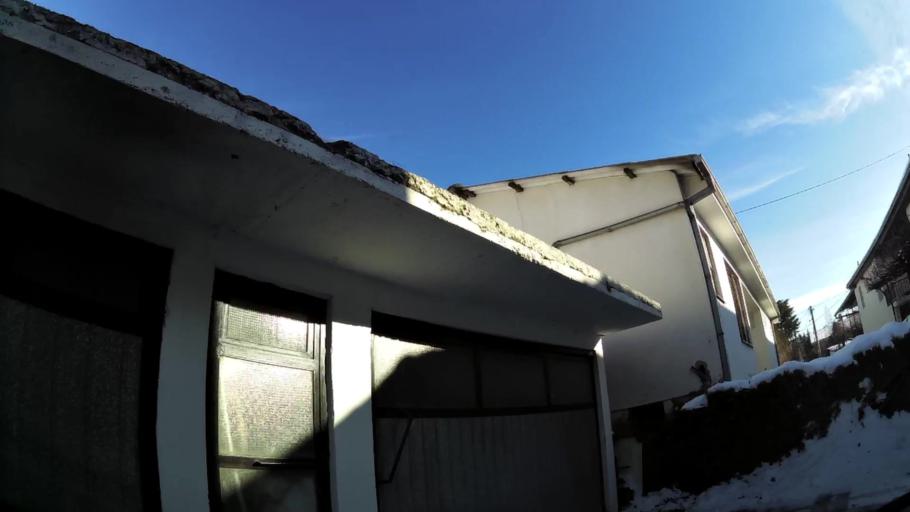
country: MK
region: Saraj
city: Saraj
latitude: 42.0066
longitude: 21.3454
